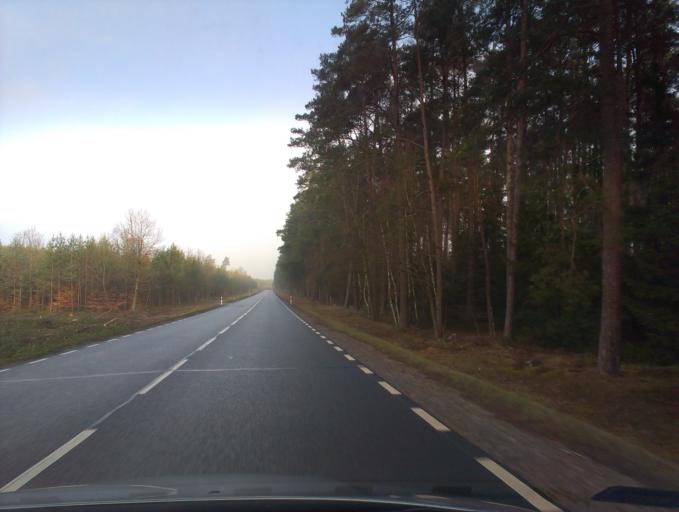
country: PL
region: West Pomeranian Voivodeship
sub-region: Powiat koszalinski
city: Sianow
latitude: 54.0618
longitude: 16.4105
